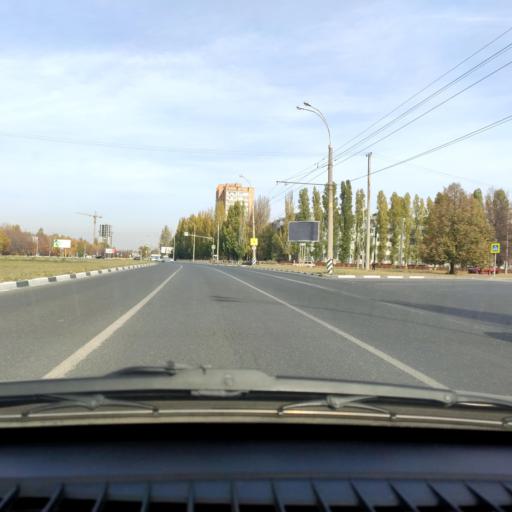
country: RU
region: Samara
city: Tol'yatti
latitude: 53.5179
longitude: 49.2953
